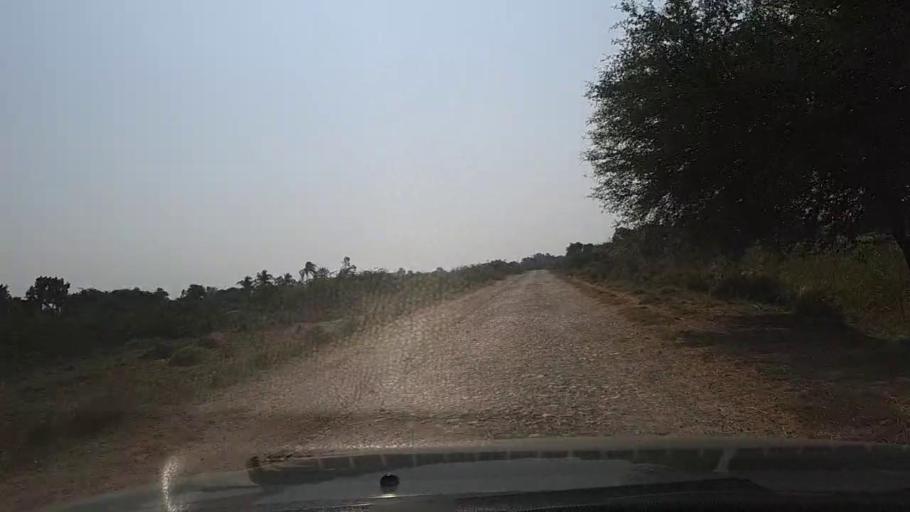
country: PK
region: Sindh
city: Mirpur Sakro
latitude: 24.4019
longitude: 67.6676
